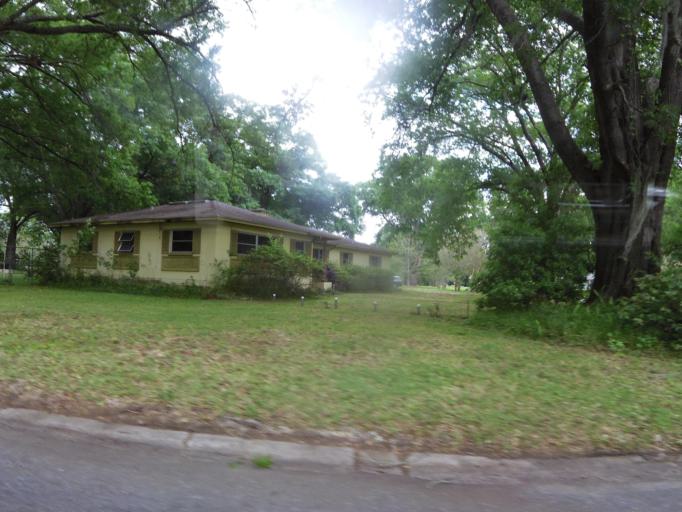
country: US
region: Florida
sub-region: Duval County
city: Jacksonville
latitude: 30.2940
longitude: -81.7352
